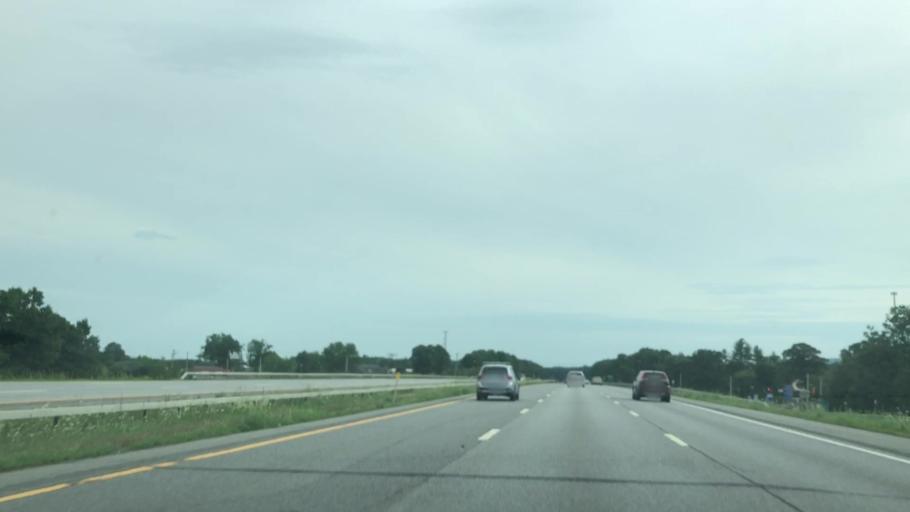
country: US
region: New York
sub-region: Warren County
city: West Glens Falls
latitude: 43.2999
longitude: -73.6785
